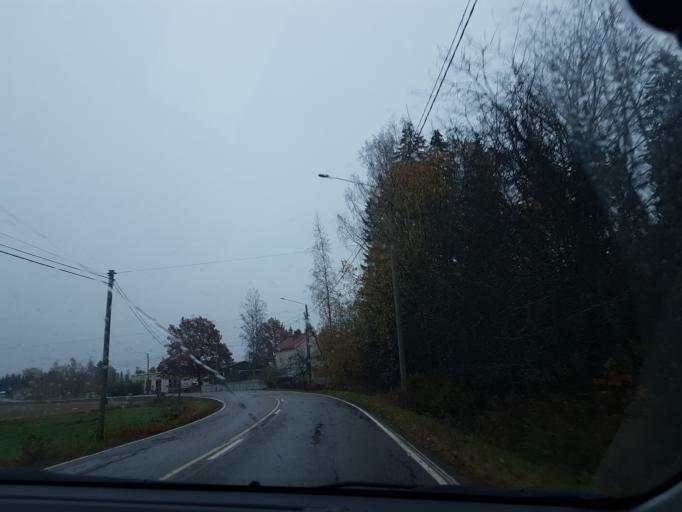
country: FI
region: Uusimaa
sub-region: Helsinki
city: Maentsaelae
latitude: 60.6136
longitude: 25.2228
